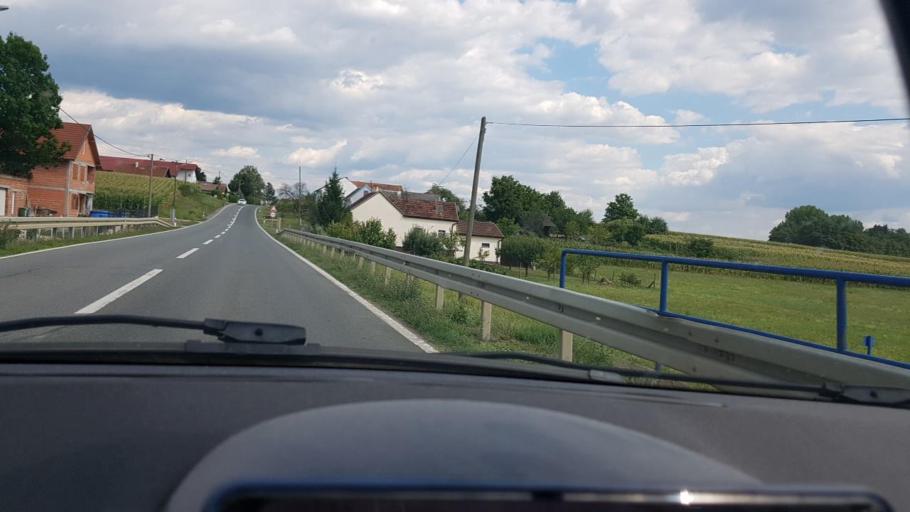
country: HR
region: Bjelovarsko-Bilogorska
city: Zdralovi
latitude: 45.8681
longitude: 16.9065
